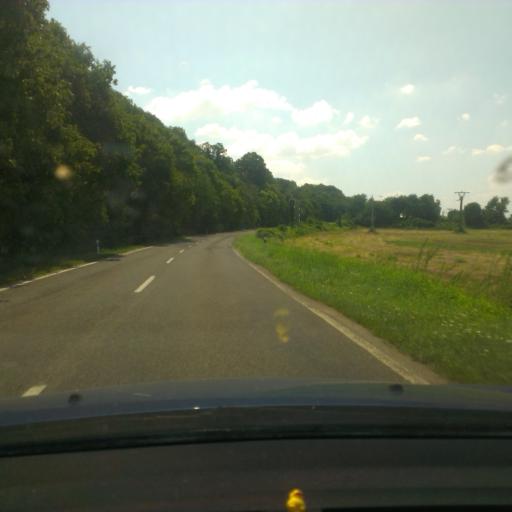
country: SK
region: Trnavsky
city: Hlohovec
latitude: 48.5002
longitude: 17.8206
